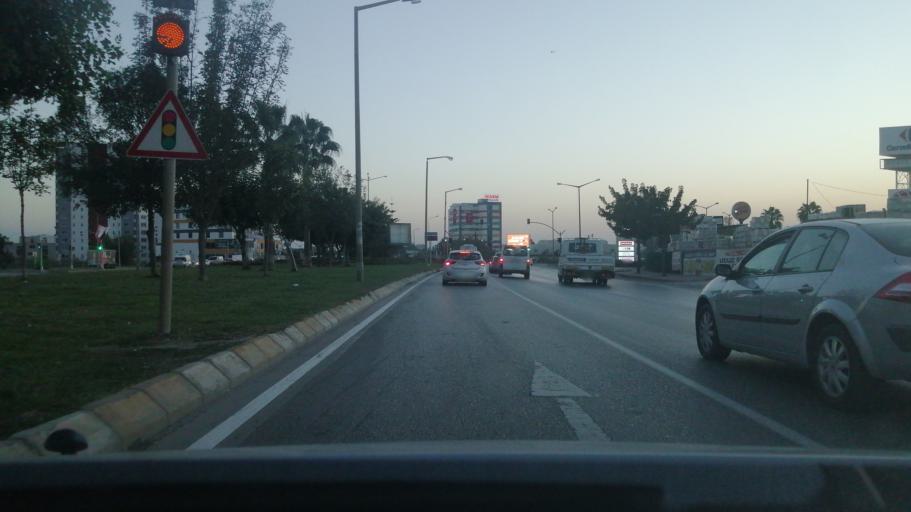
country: TR
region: Adana
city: Seyhan
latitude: 37.0168
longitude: 35.2513
